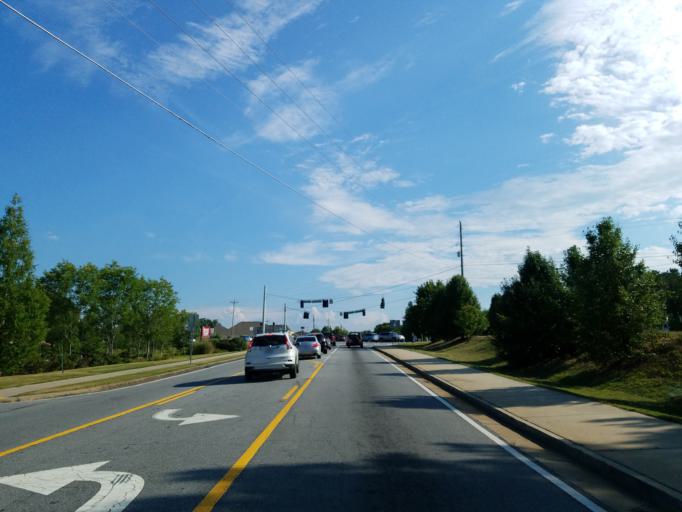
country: US
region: Georgia
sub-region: Fulton County
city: Roswell
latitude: 34.0829
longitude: -84.3569
